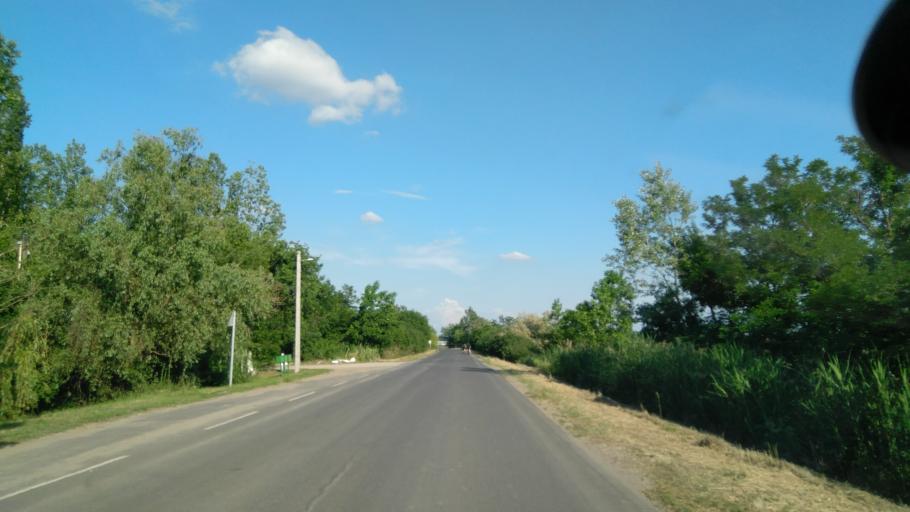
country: HU
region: Bekes
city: Gyula
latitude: 46.6582
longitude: 21.2115
